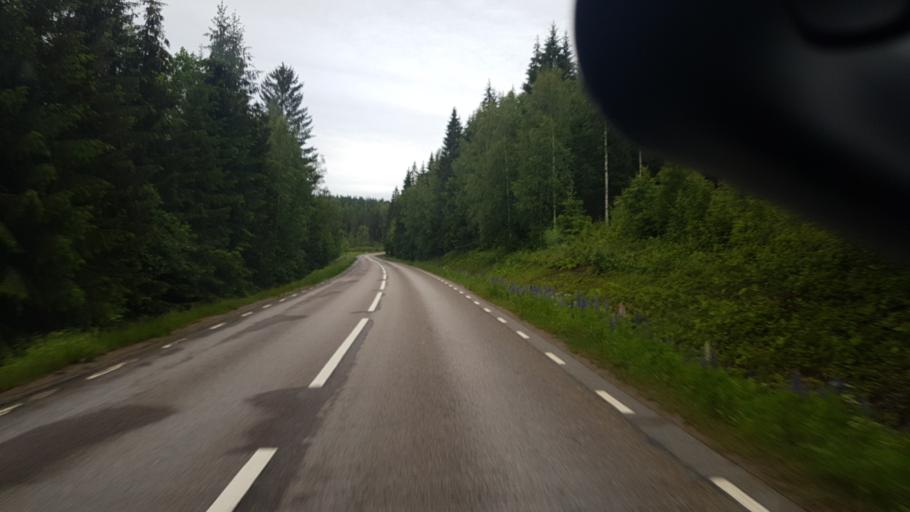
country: SE
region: Vaermland
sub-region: Eda Kommun
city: Amotfors
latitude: 59.6747
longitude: 12.3853
